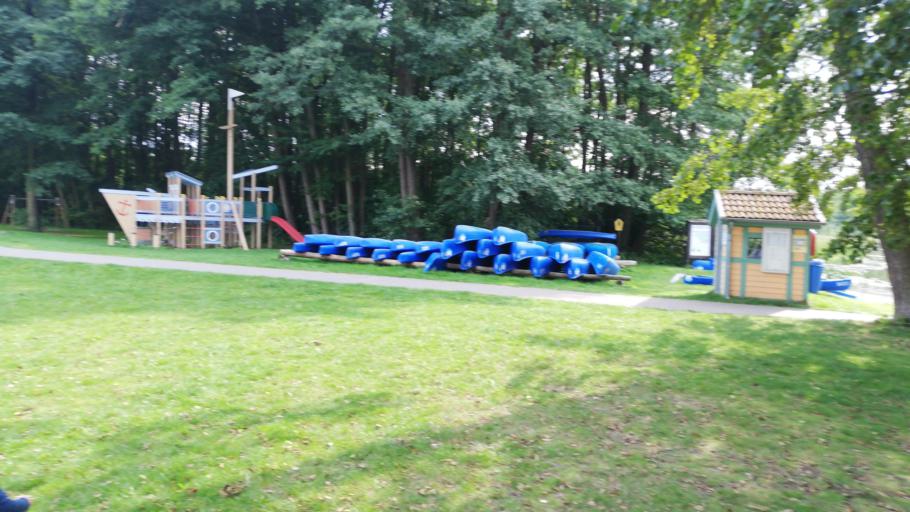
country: DE
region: Brandenburg
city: Rheinsberg
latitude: 53.1163
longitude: 12.8856
